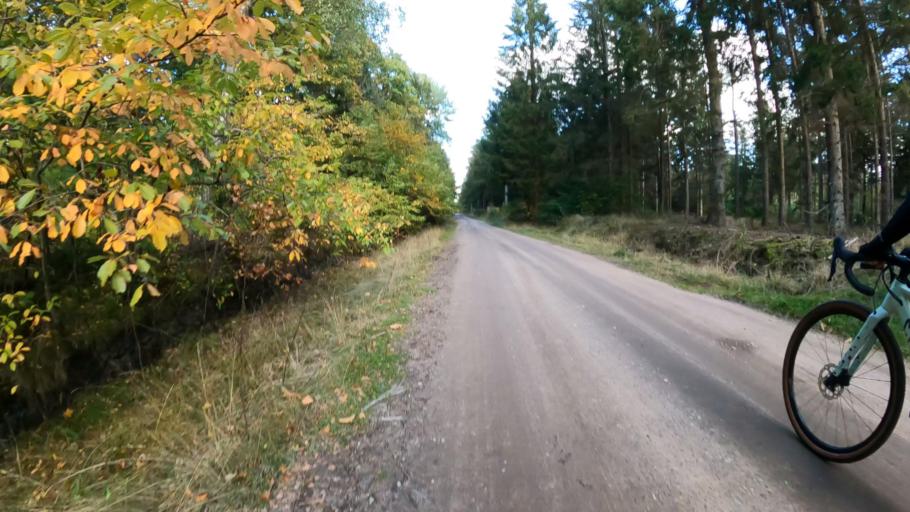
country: DE
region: Schleswig-Holstein
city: Heidmuhlen
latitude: 53.9384
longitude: 10.0849
